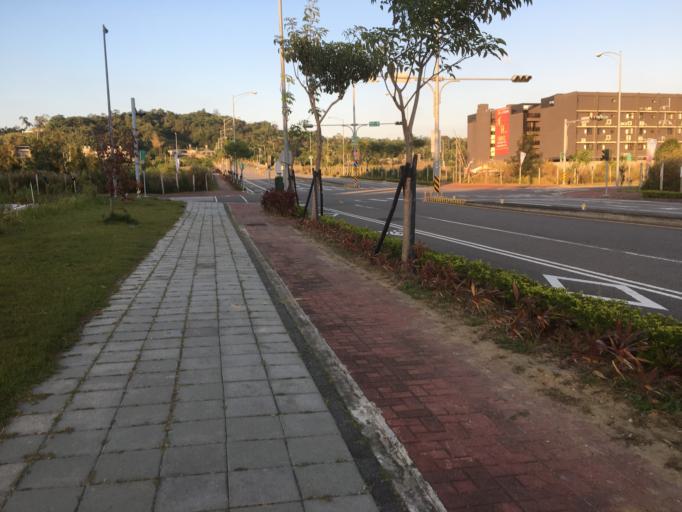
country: TW
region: Taiwan
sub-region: Miaoli
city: Miaoli
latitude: 24.6107
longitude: 120.8282
